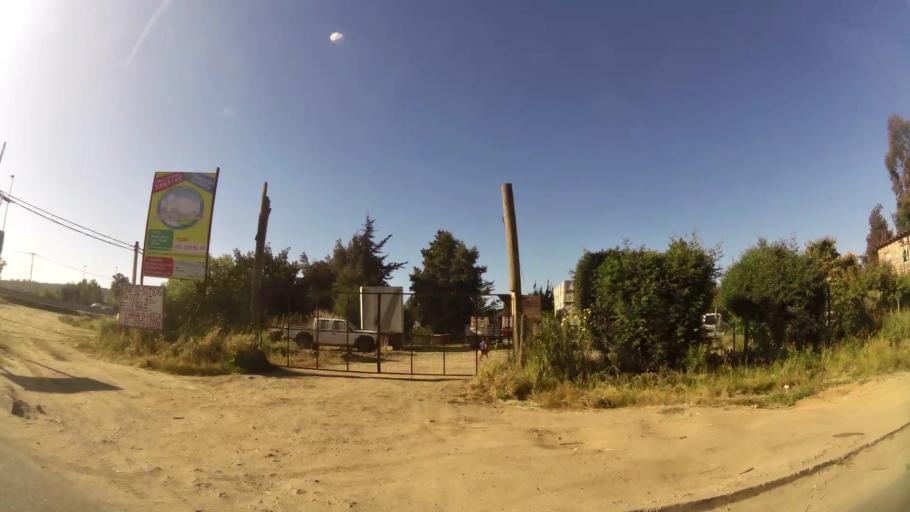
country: CL
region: Valparaiso
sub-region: Provincia de Valparaiso
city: Vina del Mar
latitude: -33.1172
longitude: -71.5599
